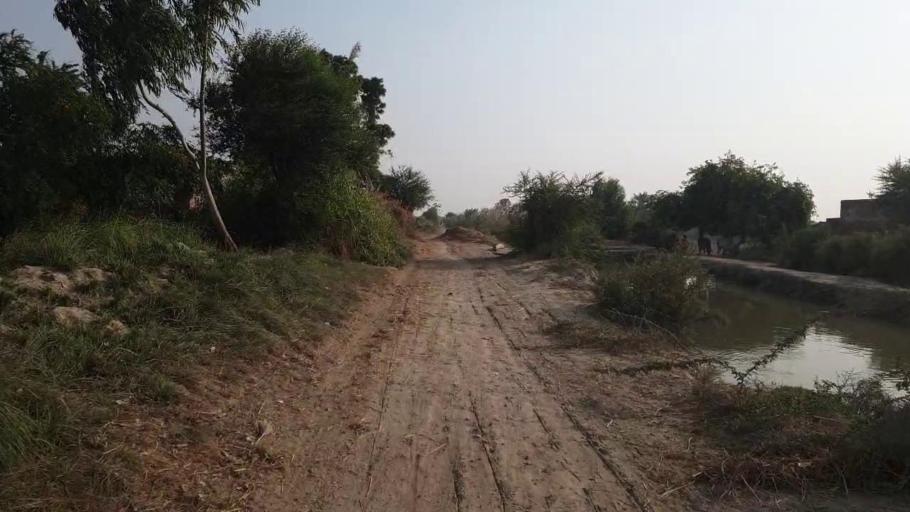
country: PK
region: Sindh
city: Tando Muhammad Khan
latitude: 25.0875
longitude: 68.3584
